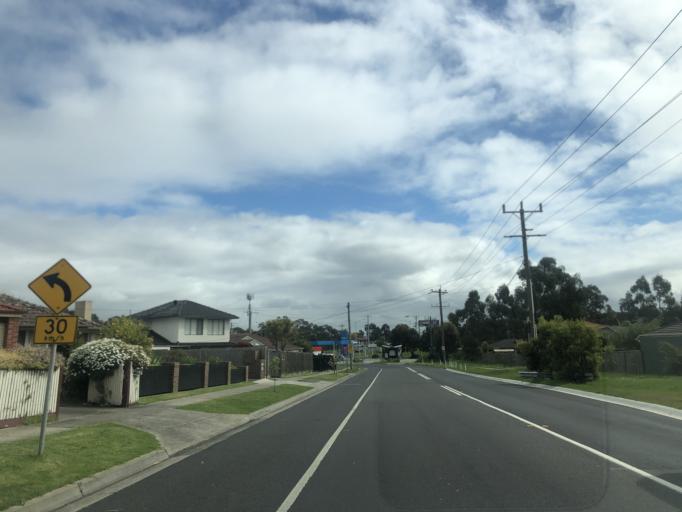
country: AU
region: Victoria
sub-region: Knox
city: Rowville
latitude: -37.9307
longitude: 145.2342
